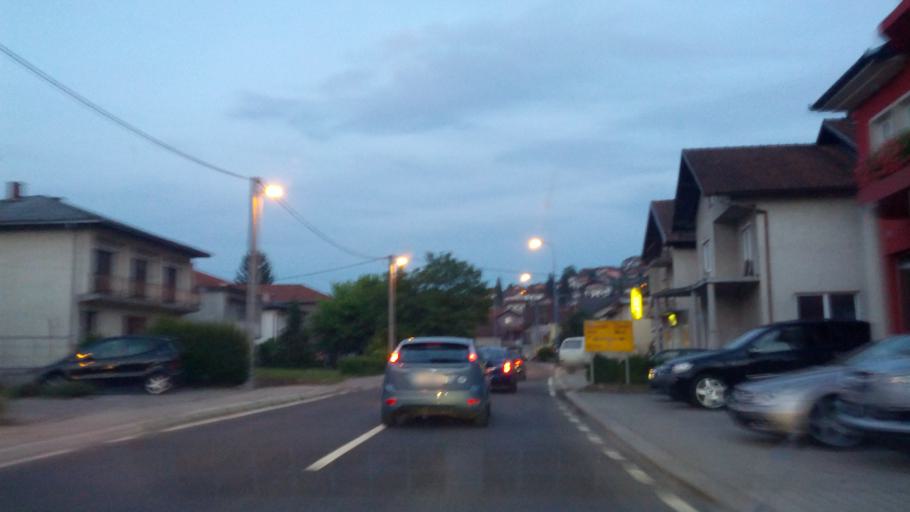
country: BA
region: Federation of Bosnia and Herzegovina
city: Bosanska Krupa
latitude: 44.8801
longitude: 16.1499
